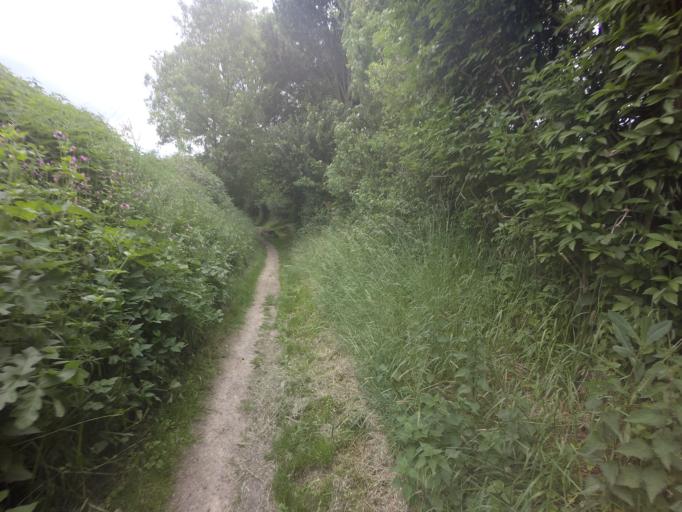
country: NL
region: Limburg
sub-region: Gemeente Voerendaal
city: Ubachsberg
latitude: 50.8081
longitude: 5.9386
